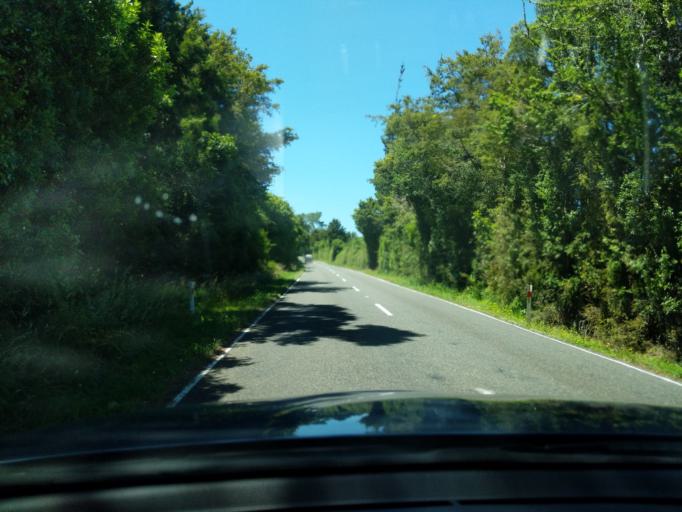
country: NZ
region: Tasman
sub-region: Tasman District
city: Takaka
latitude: -40.7240
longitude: 172.5970
